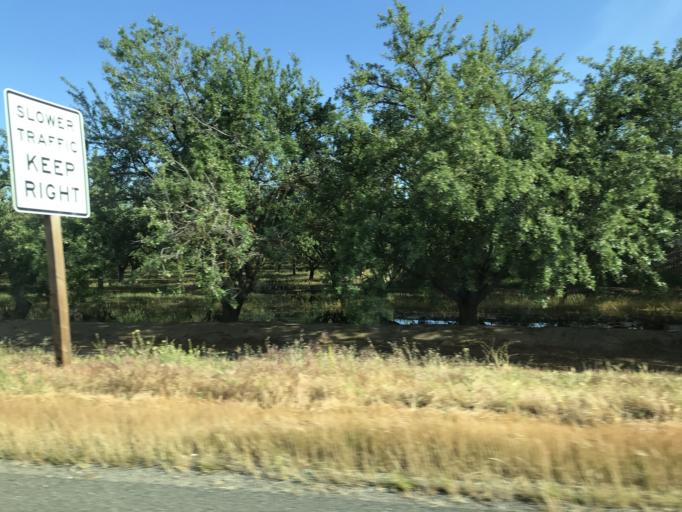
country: US
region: California
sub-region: Fresno County
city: West Park
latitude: 36.7354
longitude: -119.8994
